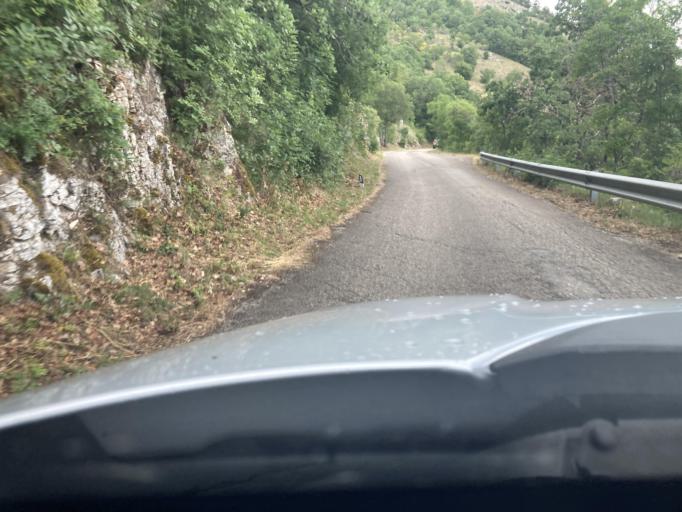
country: IT
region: Abruzzo
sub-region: Provincia dell' Aquila
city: Fossa
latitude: 42.2853
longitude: 13.4930
